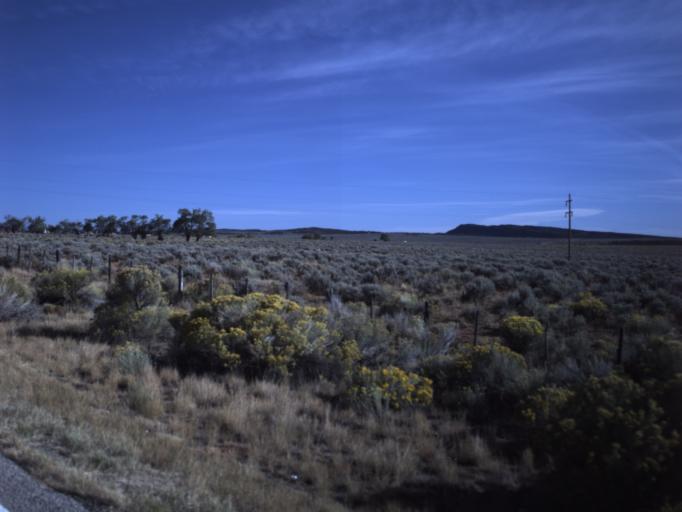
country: US
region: Utah
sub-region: Grand County
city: Moab
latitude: 38.3120
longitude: -109.3003
